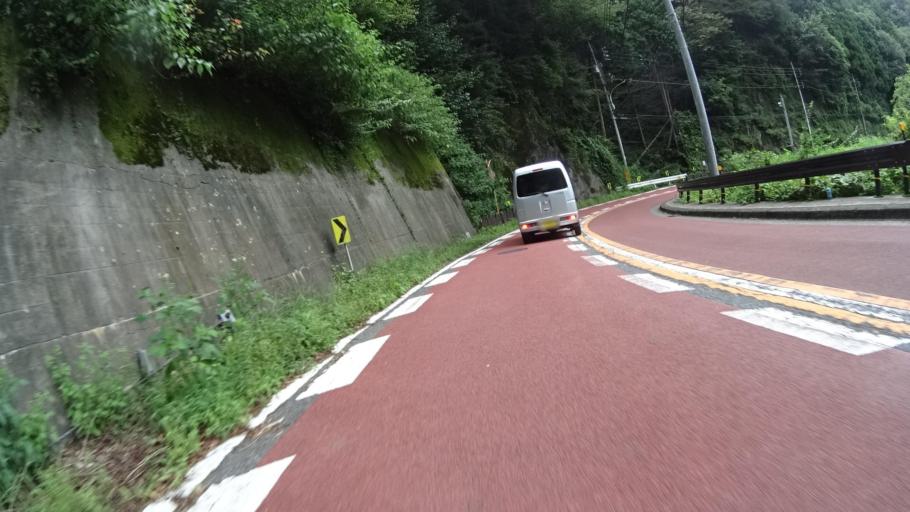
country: JP
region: Yamanashi
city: Uenohara
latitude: 35.7034
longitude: 139.1062
